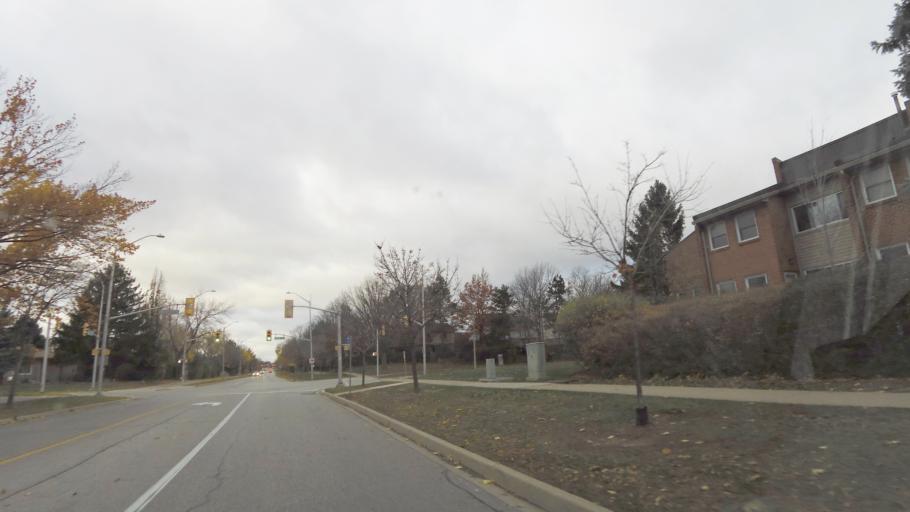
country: CA
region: Ontario
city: Oakville
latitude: 43.4760
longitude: -79.6888
